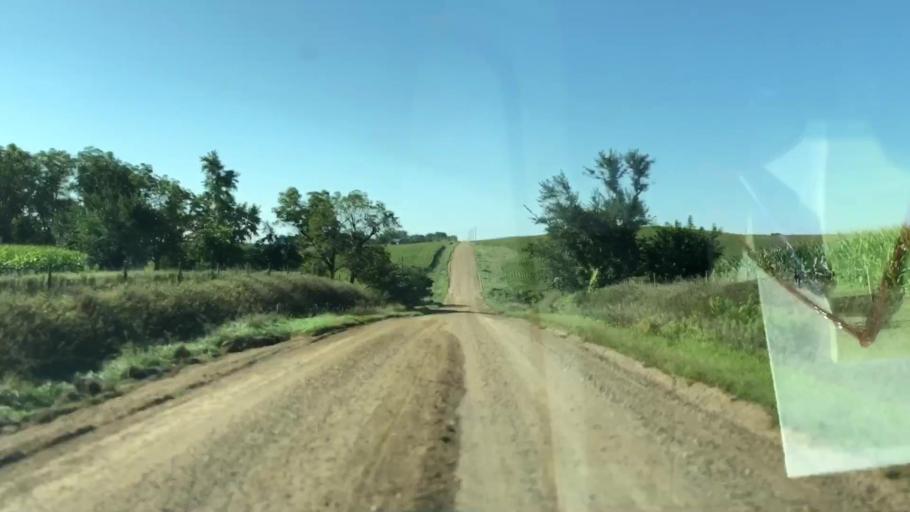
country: US
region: Iowa
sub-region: Woodbury County
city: Sergeant Bluff
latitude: 42.4678
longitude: -96.2525
